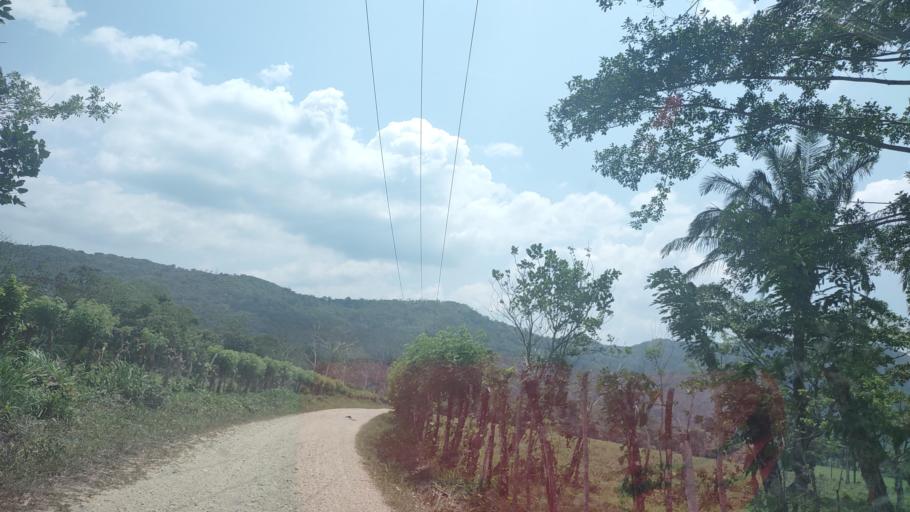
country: MX
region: Chiapas
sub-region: Tecpatan
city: Raudales Malpaso
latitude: 17.2759
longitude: -93.8709
